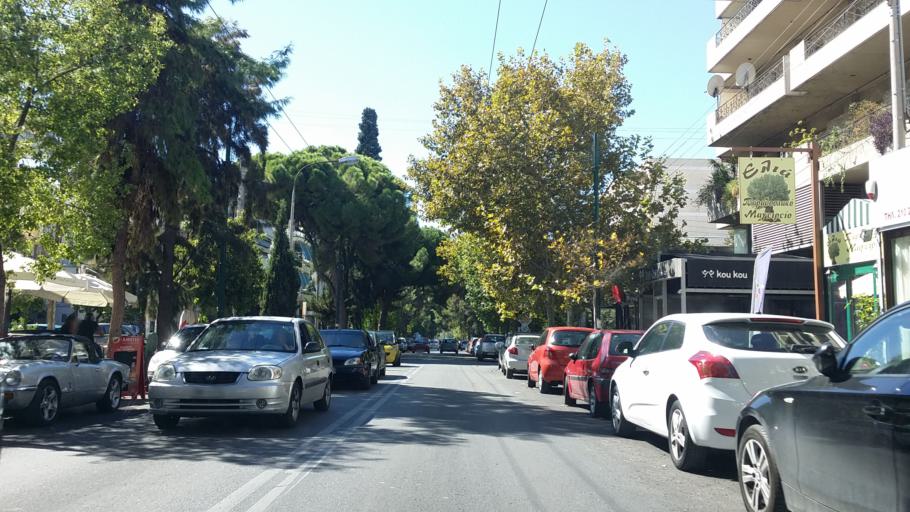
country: GR
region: Attica
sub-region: Nomarchia Athinas
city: Nea Filadelfeia
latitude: 38.0309
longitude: 23.7360
